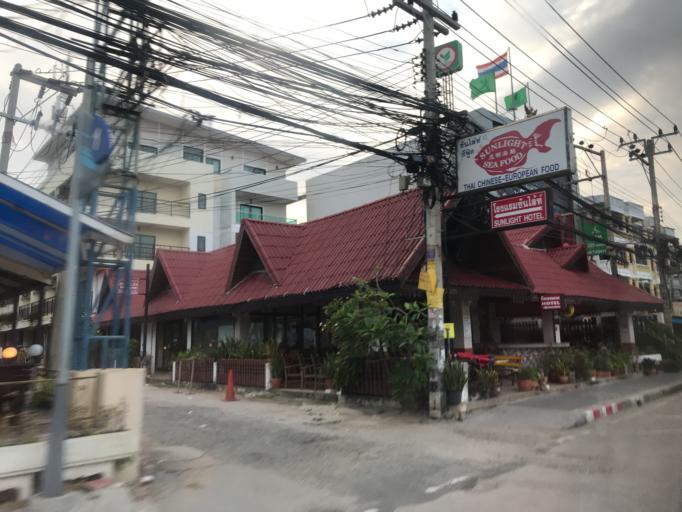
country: TH
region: Chon Buri
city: Phatthaya
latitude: 12.8977
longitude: 100.8680
